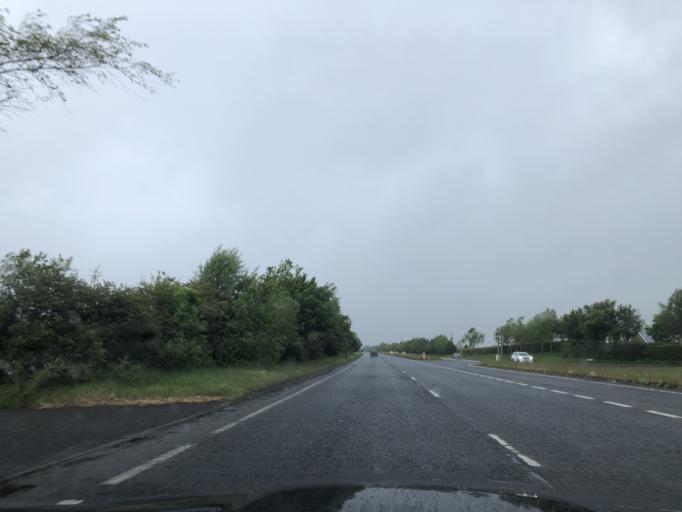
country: GB
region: Northern Ireland
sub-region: Ballymena District
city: Ballymena
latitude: 54.8307
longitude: -6.2662
